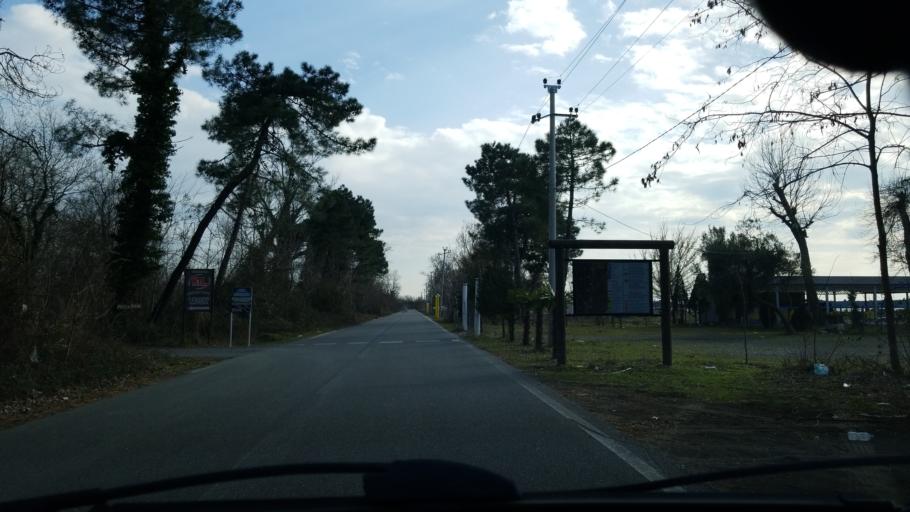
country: AL
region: Lezhe
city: Shengjin
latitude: 41.7790
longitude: 19.6033
